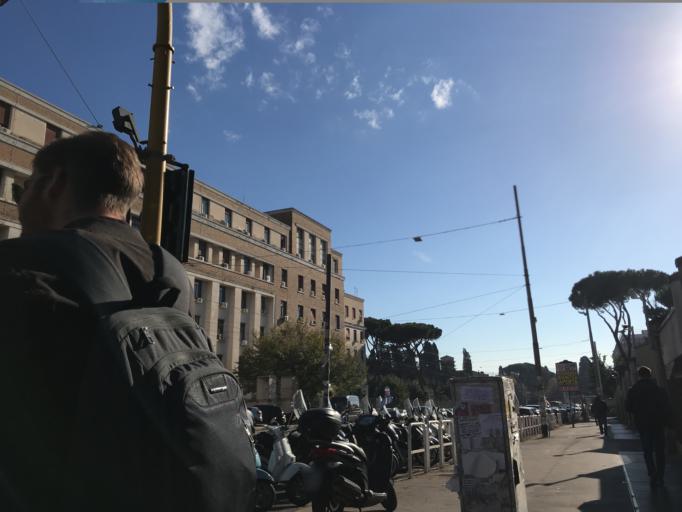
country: IT
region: Latium
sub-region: Citta metropolitana di Roma Capitale
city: Rome
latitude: 41.9043
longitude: 12.5173
